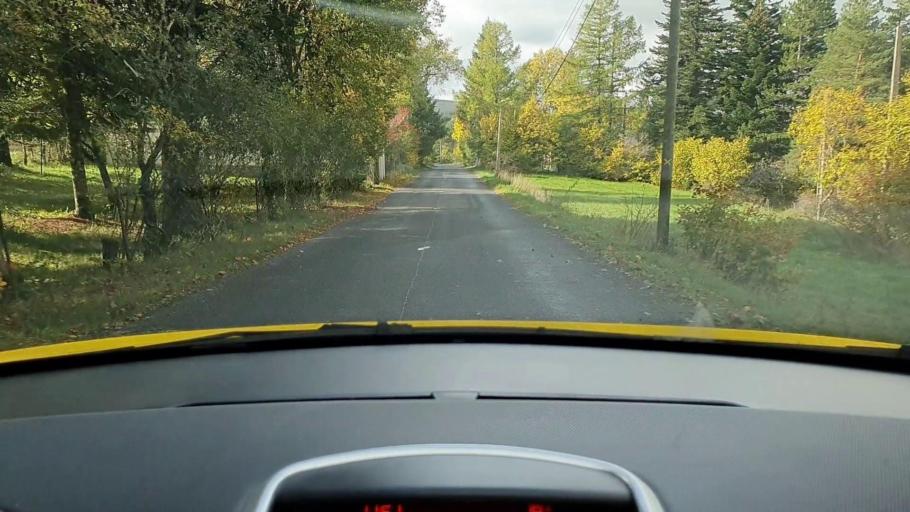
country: FR
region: Languedoc-Roussillon
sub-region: Departement de la Lozere
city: Meyrueis
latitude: 44.1138
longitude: 3.4716
